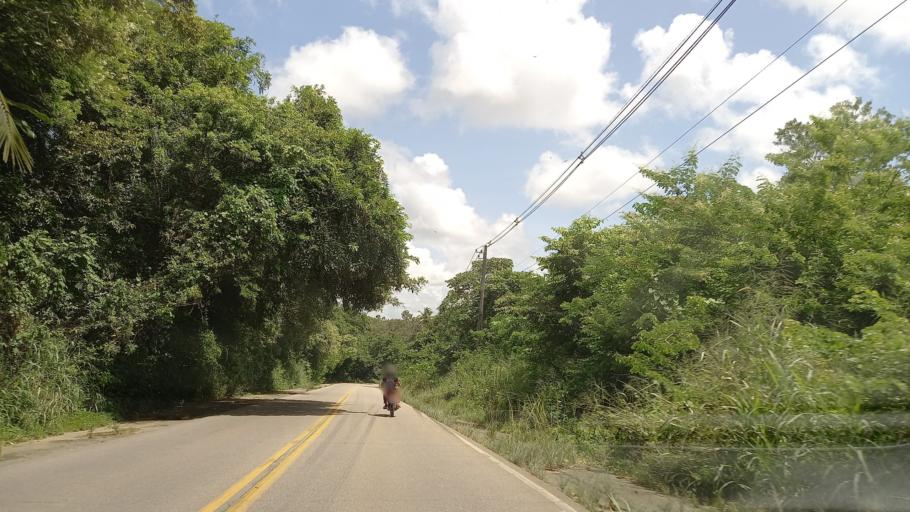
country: BR
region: Pernambuco
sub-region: Rio Formoso
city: Rio Formoso
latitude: -8.6569
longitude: -35.1414
